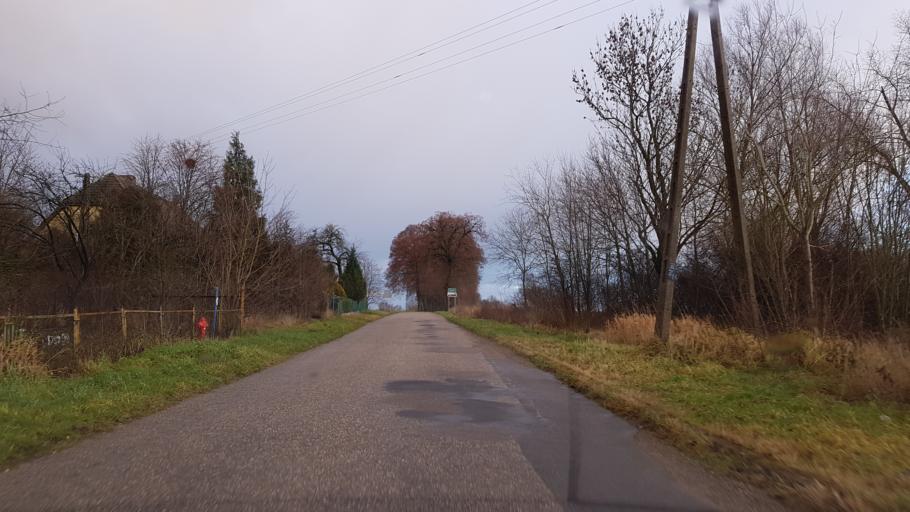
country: PL
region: West Pomeranian Voivodeship
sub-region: Powiat swidwinski
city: Rabino
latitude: 53.9445
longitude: 15.9209
